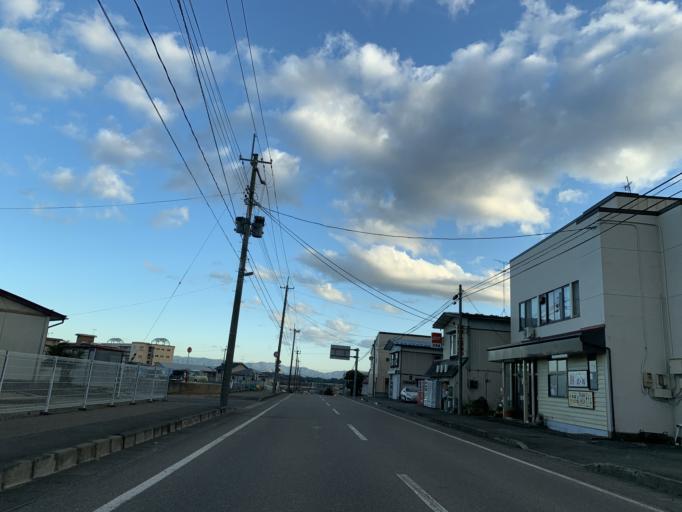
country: JP
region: Iwate
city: Kitakami
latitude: 39.2607
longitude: 141.1031
